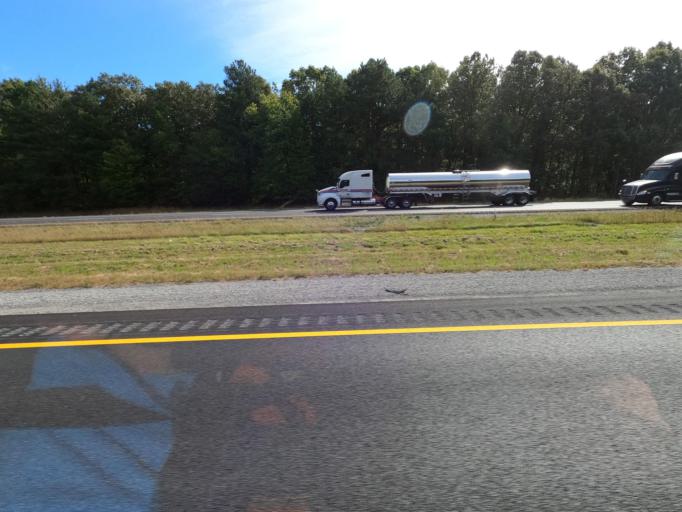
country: US
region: Tennessee
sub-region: Humphreys County
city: McEwen
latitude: 35.9576
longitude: -87.5519
